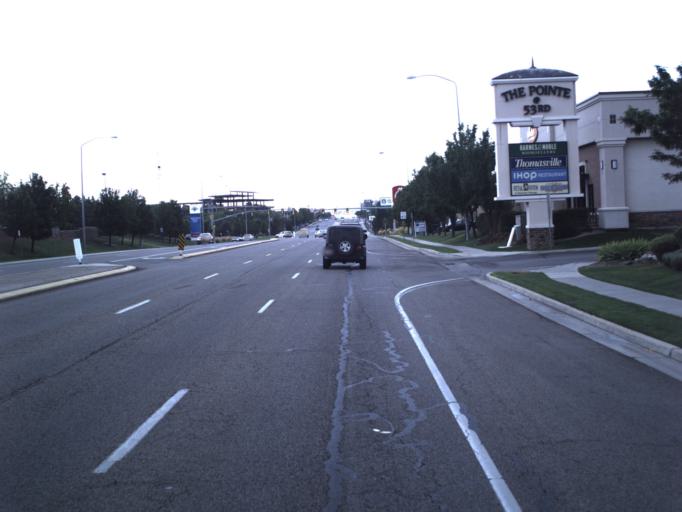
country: US
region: Utah
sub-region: Salt Lake County
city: Murray
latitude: 40.6574
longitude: -111.8882
